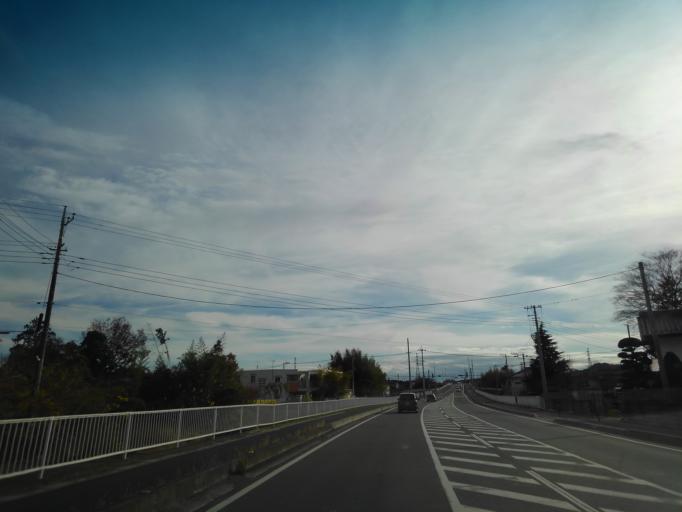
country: JP
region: Saitama
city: Morohongo
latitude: 35.9384
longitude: 139.3170
